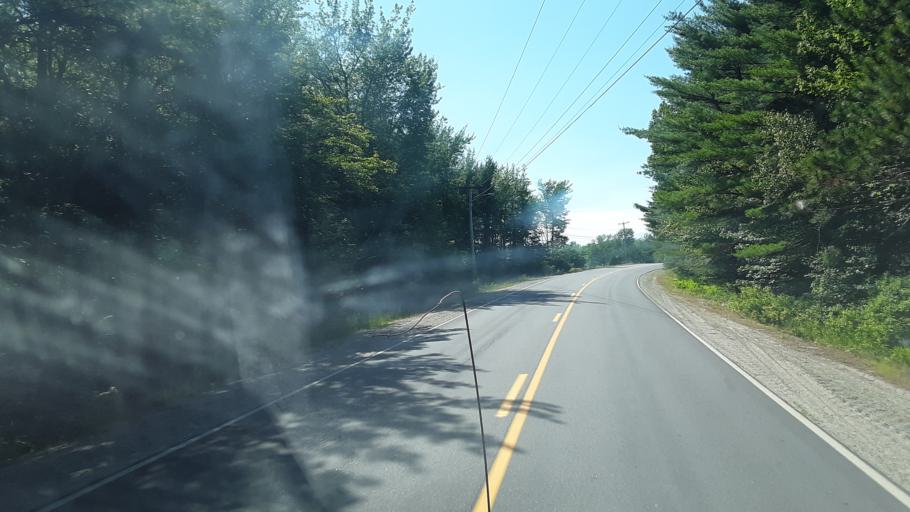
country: US
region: Maine
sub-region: Washington County
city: Cherryfield
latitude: 44.6206
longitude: -67.9330
